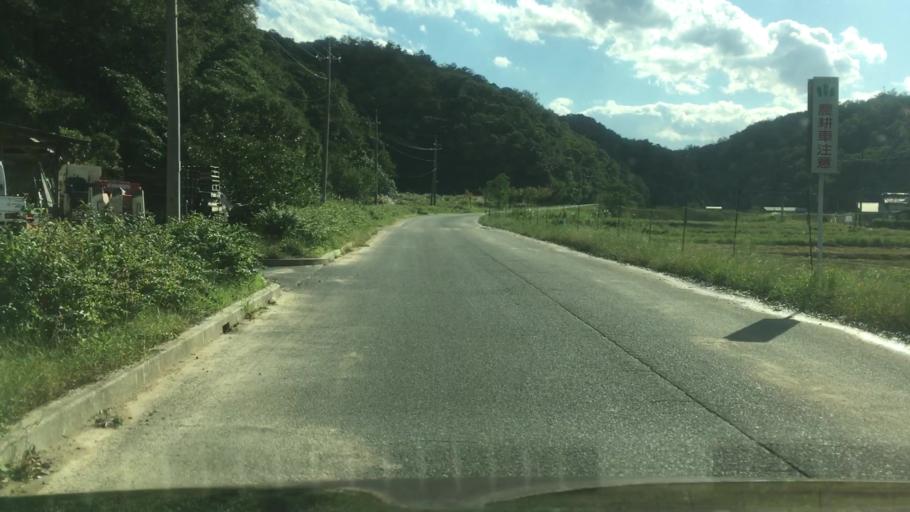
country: JP
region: Hyogo
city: Toyooka
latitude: 35.6474
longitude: 134.9646
